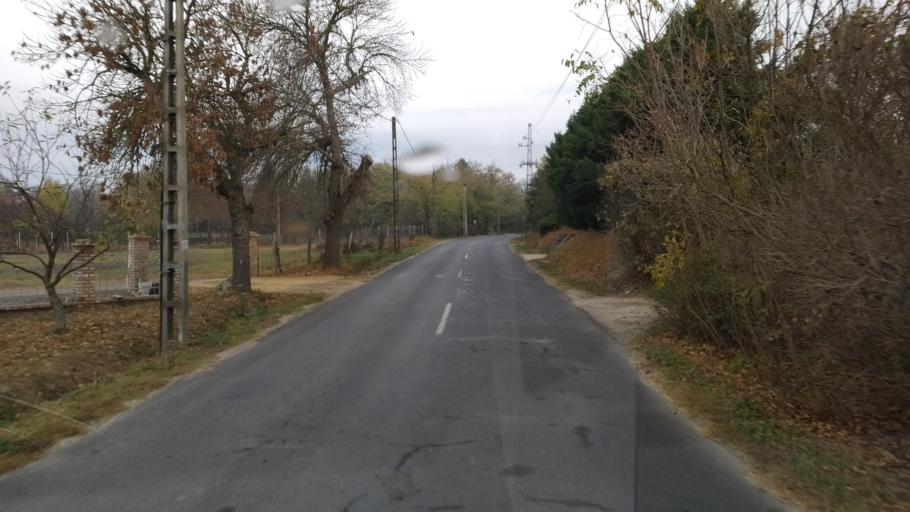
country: HU
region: Pest
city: Tahitotfalu
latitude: 47.7696
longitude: 19.0877
